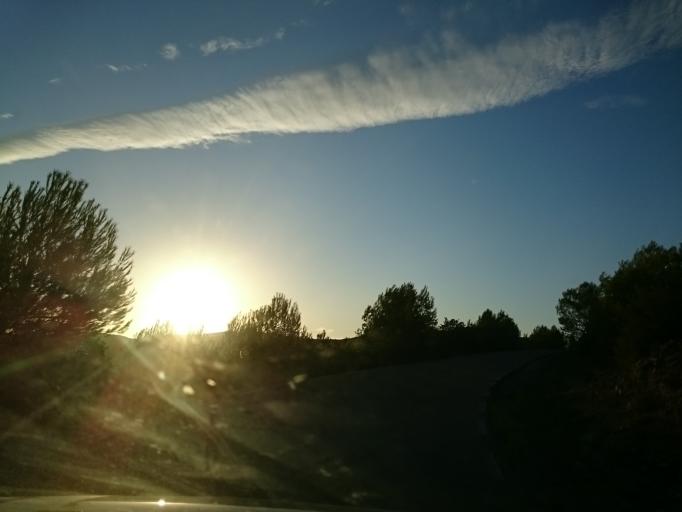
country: ES
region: Catalonia
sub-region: Provincia de Barcelona
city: Olivella
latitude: 41.3037
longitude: 1.8240
